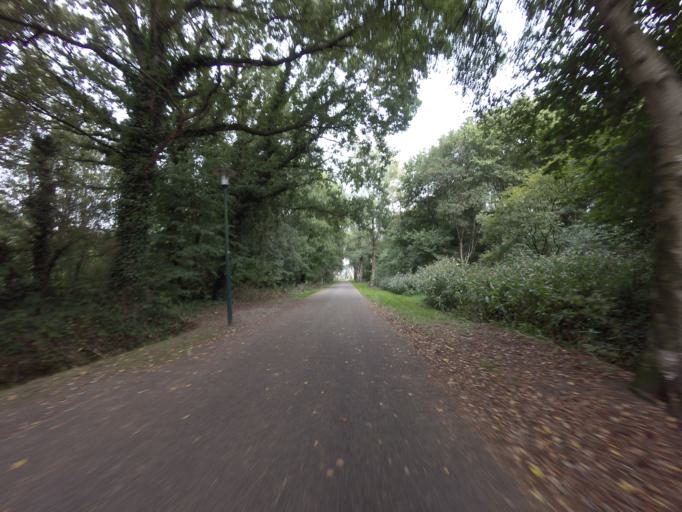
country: NL
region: Drenthe
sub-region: Gemeente Tynaarlo
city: Vries
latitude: 53.0703
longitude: 6.5800
